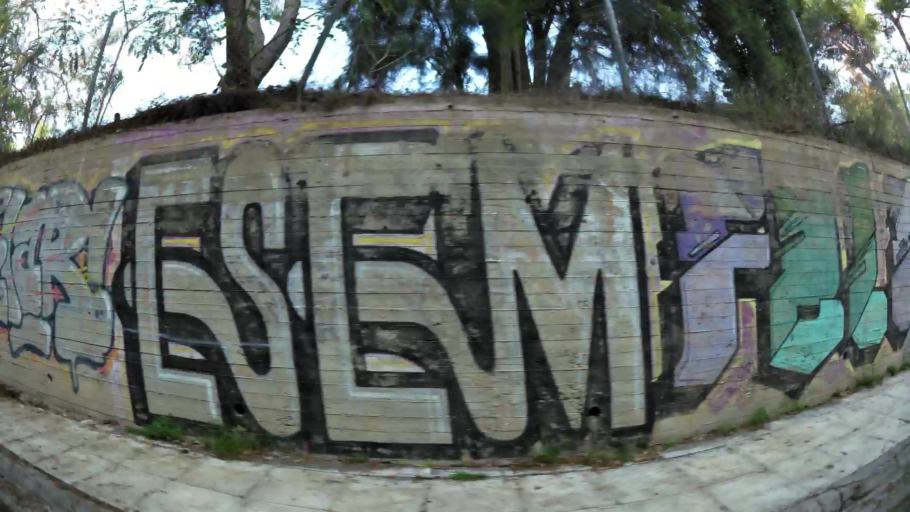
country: GR
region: Attica
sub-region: Nomarchia Athinas
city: Agia Paraskevi
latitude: 38.0073
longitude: 23.8328
